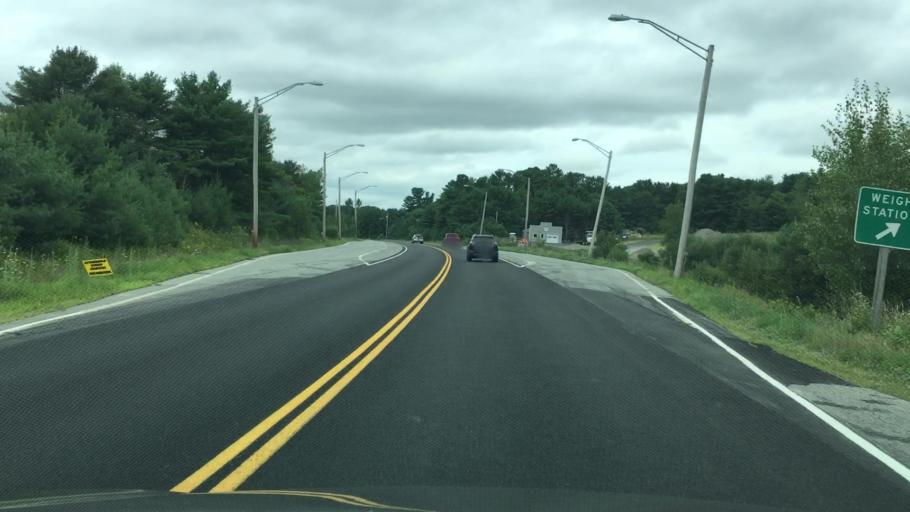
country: US
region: Maine
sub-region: Penobscot County
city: Orrington
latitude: 44.6936
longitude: -68.8127
